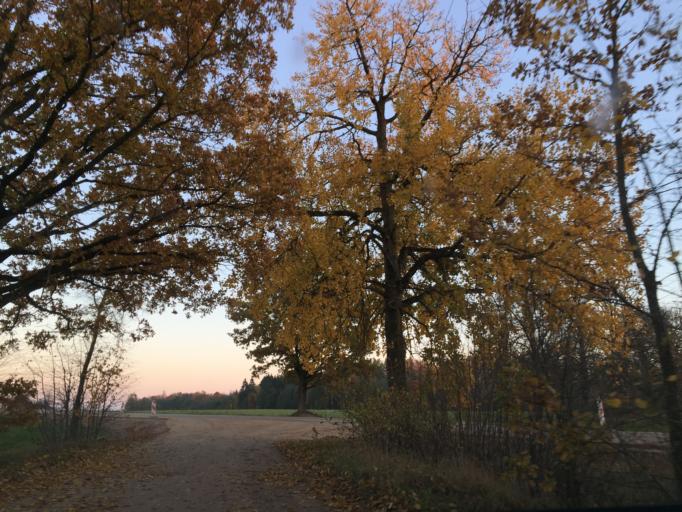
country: LT
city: Vieksniai
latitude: 56.4060
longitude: 22.5150
